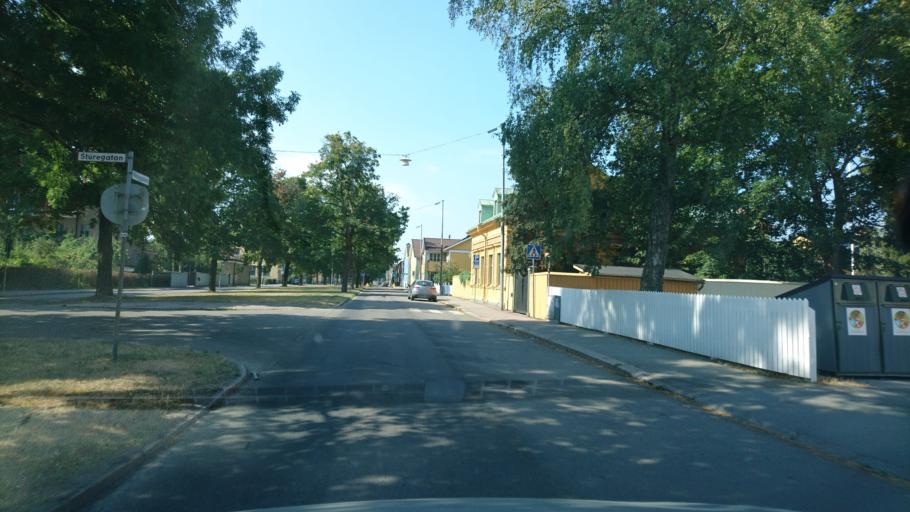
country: SE
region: Uppsala
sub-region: Uppsala Kommun
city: Uppsala
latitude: 59.8661
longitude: 17.6211
